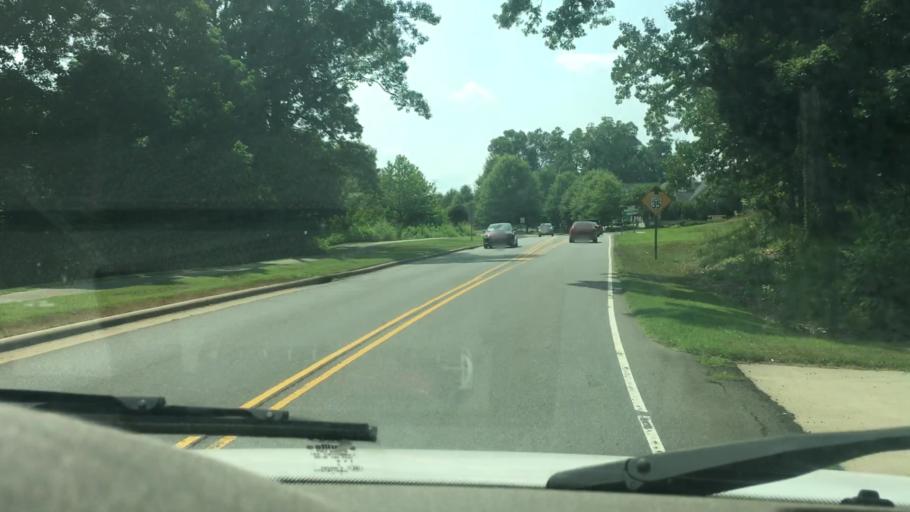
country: US
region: North Carolina
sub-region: Mecklenburg County
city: Huntersville
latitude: 35.4070
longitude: -80.8998
